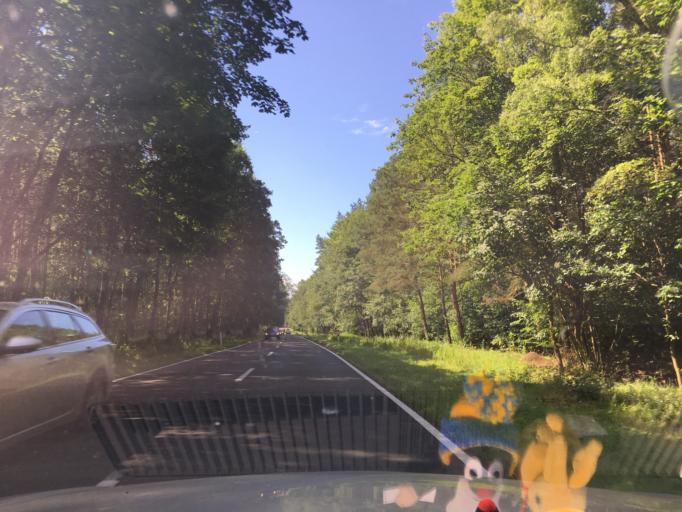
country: PL
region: West Pomeranian Voivodeship
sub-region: Powiat kamienski
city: Kamien Pomorski
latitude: 53.8696
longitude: 14.7721
